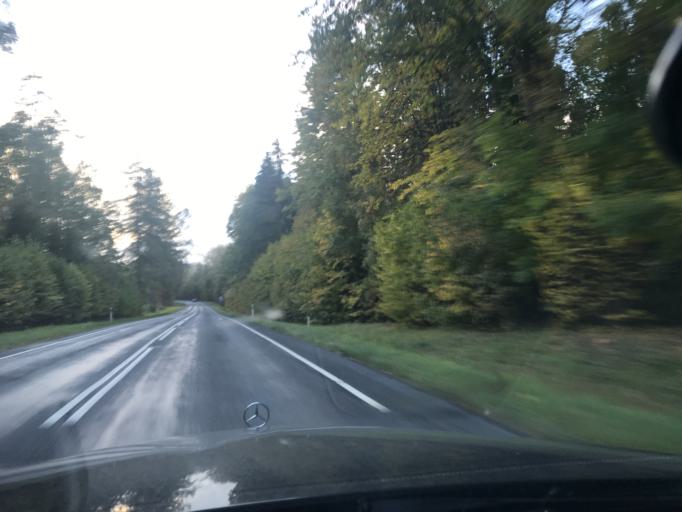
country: EE
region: Vorumaa
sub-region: Antsla vald
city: Vana-Antsla
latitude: 57.8823
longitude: 26.5690
